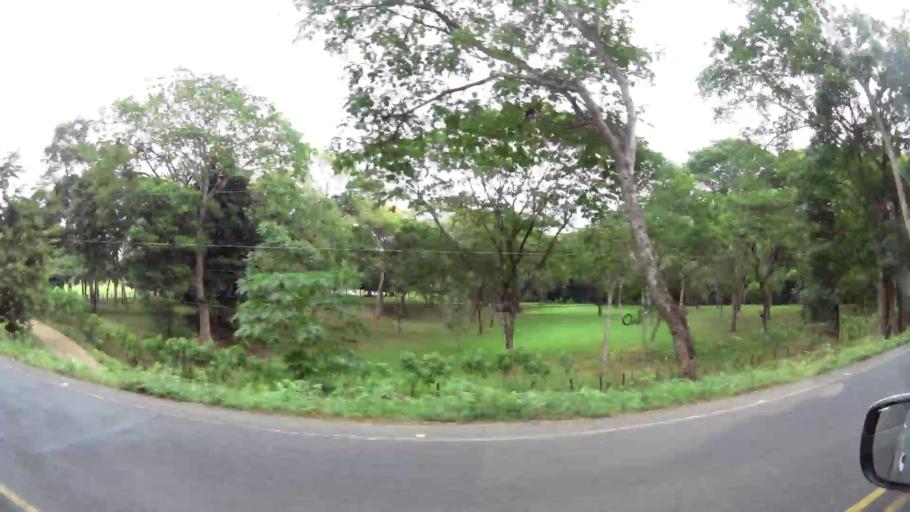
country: CR
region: Guanacaste
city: Juntas
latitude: 10.1630
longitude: -84.9184
